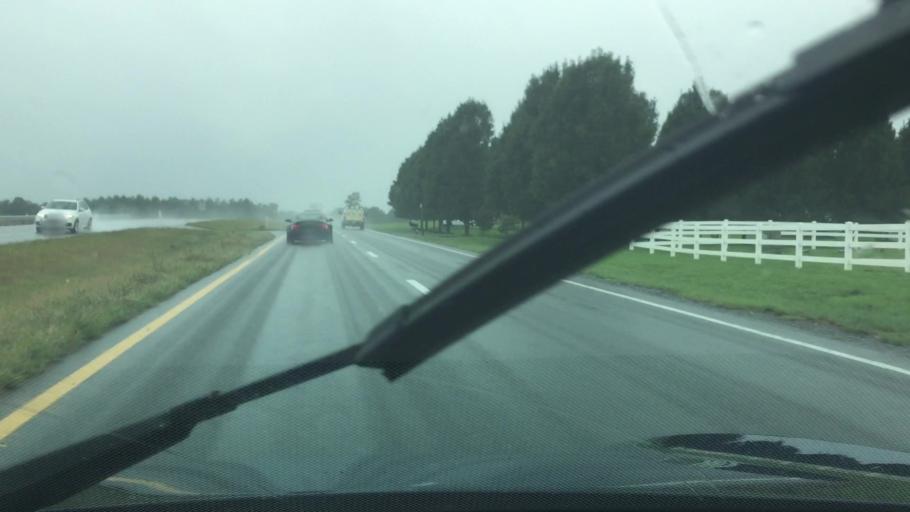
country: US
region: Virginia
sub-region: City of Bedford
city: Bedford
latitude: 37.3159
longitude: -79.4106
